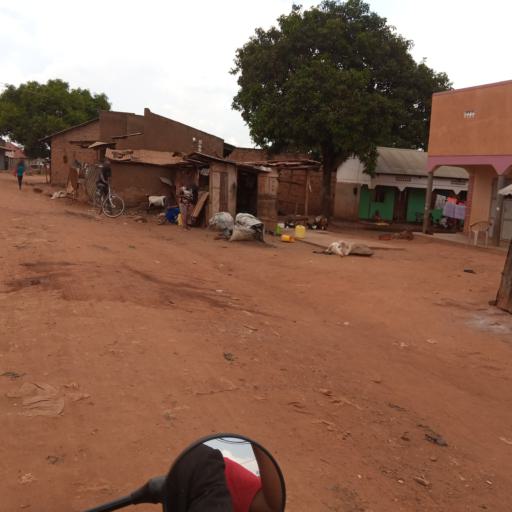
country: UG
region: Eastern Region
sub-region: Mbale District
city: Mbale
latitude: 1.0938
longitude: 34.1699
